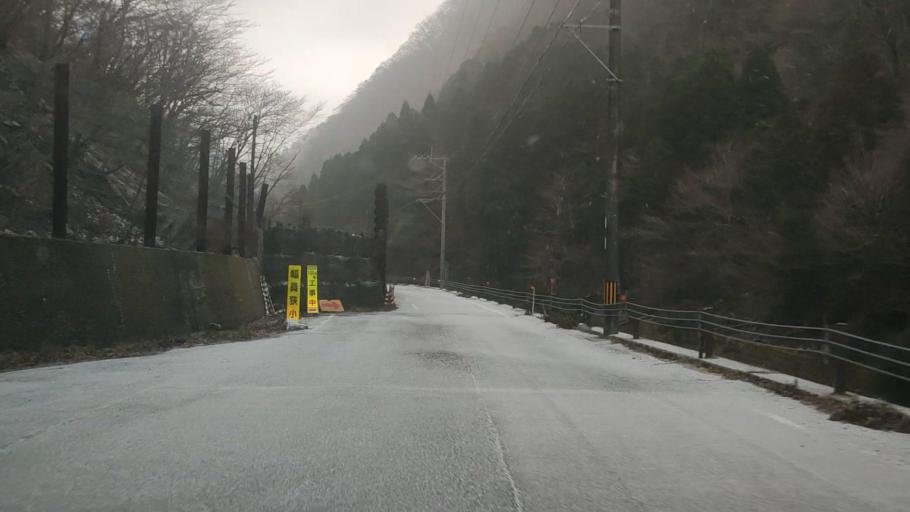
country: JP
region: Kumamoto
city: Matsubase
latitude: 32.5555
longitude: 130.9227
